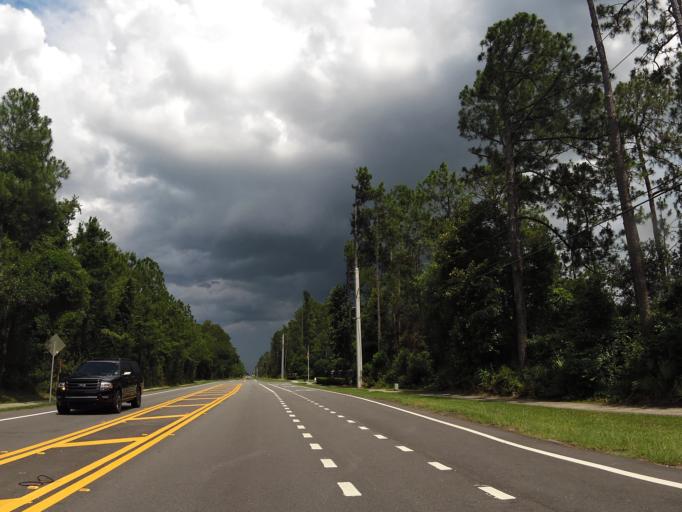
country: US
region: Florida
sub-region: Saint Johns County
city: Fruit Cove
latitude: 30.0641
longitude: -81.6596
